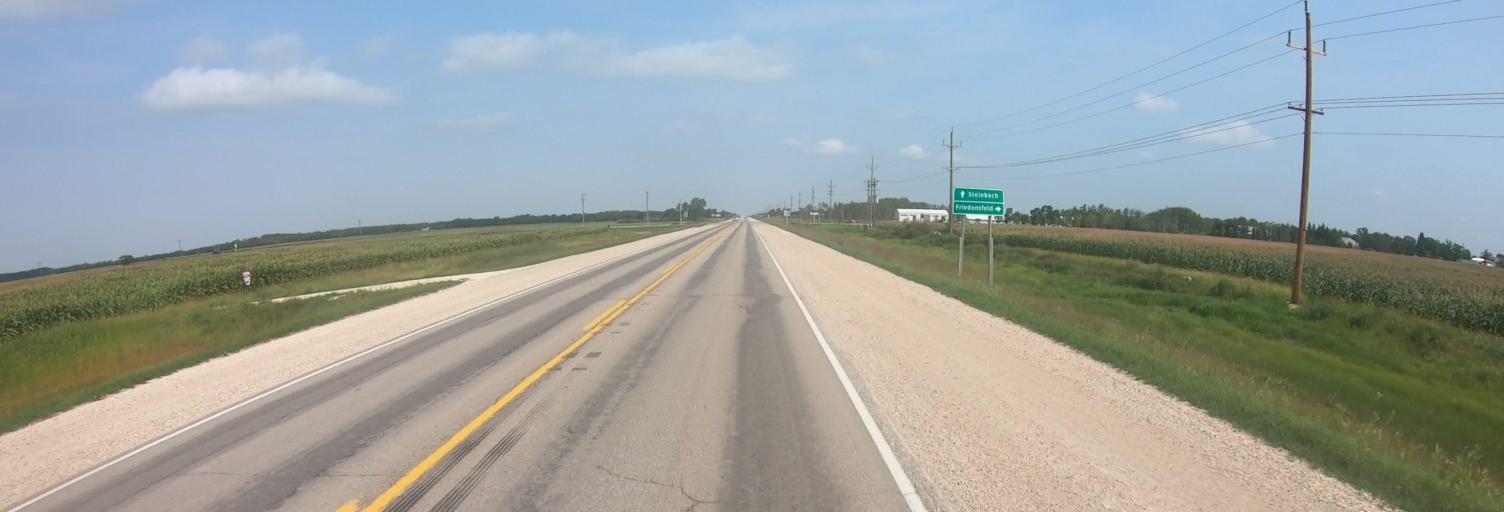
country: CA
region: Manitoba
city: Steinbach
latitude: 49.4711
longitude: -96.6911
